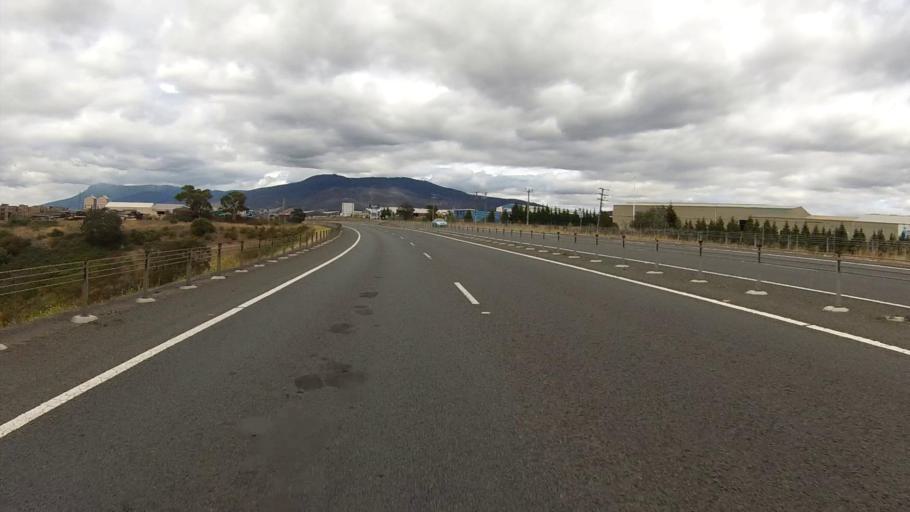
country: AU
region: Tasmania
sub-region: Brighton
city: Bridgewater
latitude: -42.7176
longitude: 147.2393
